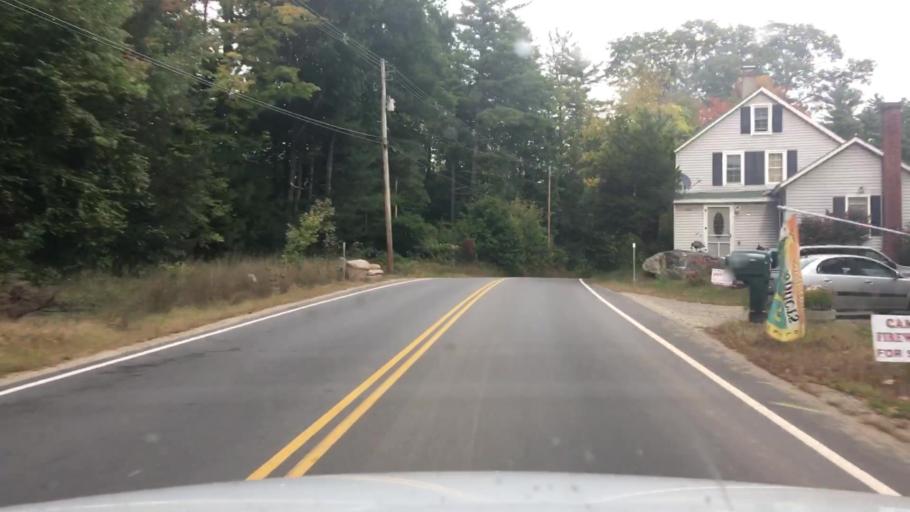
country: US
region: New Hampshire
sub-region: Carroll County
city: Wolfeboro
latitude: 43.5384
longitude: -71.2951
